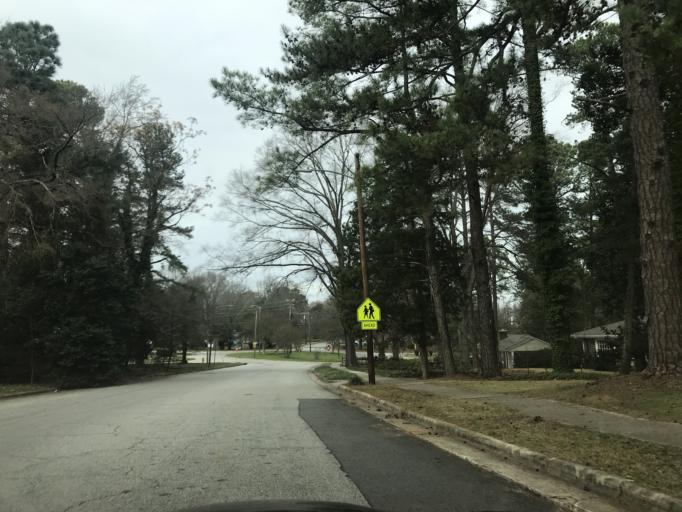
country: US
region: North Carolina
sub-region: Wake County
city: Raleigh
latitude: 35.7824
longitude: -78.6106
